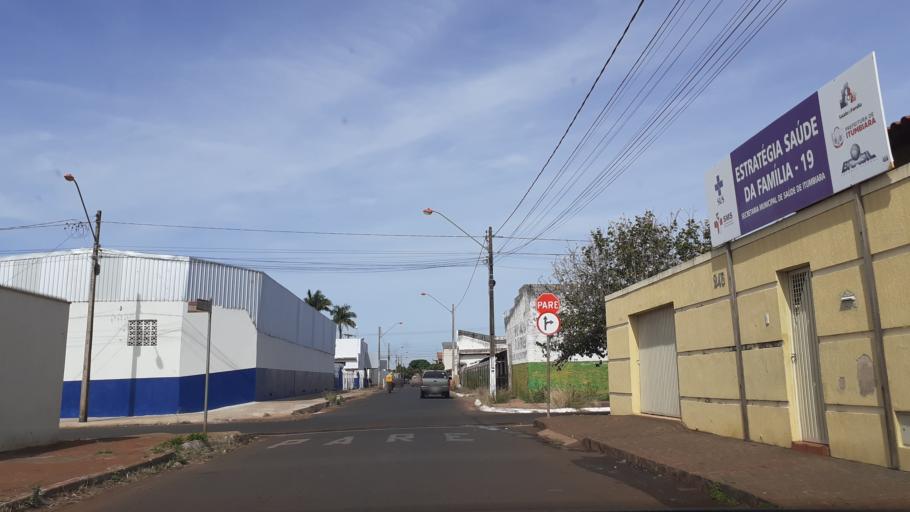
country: BR
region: Goias
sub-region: Itumbiara
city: Itumbiara
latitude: -18.4161
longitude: -49.2295
